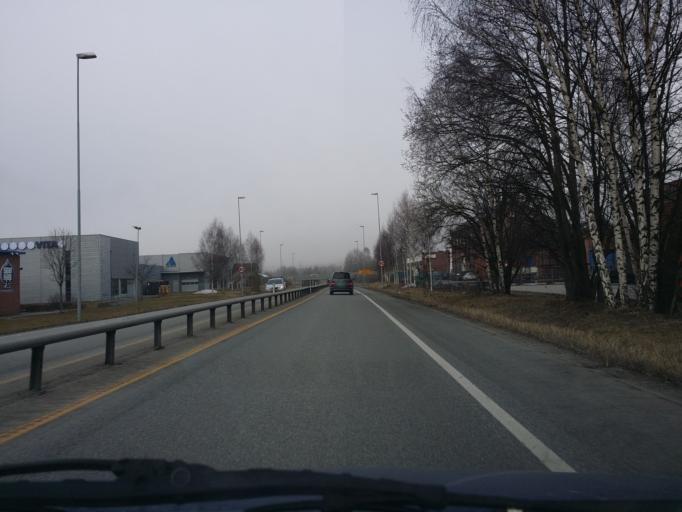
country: NO
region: Buskerud
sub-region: Nedre Eiker
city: Mjondalen
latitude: 59.7494
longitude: 10.0321
